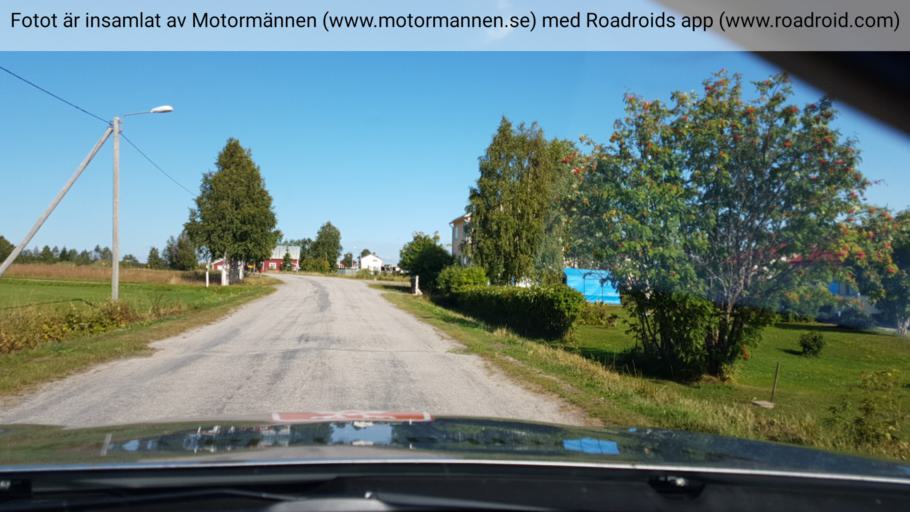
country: SE
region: Norrbotten
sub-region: Kalix Kommun
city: Kalix
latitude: 66.1801
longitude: 23.2132
